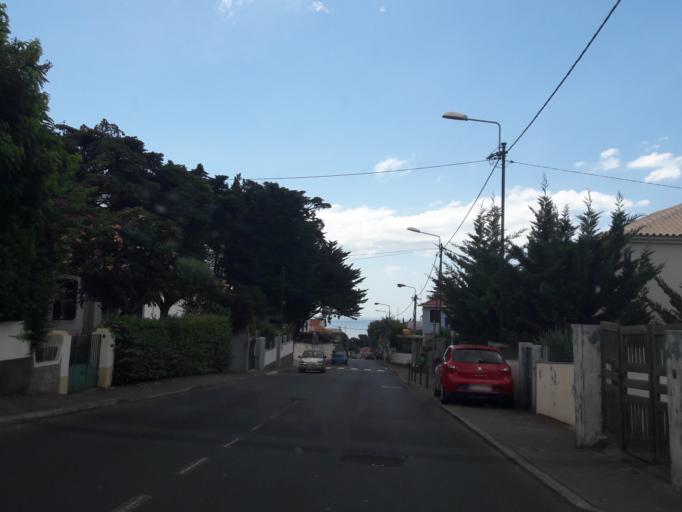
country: PT
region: Madeira
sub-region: Funchal
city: Nossa Senhora do Monte
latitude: 32.6608
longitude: -16.9231
